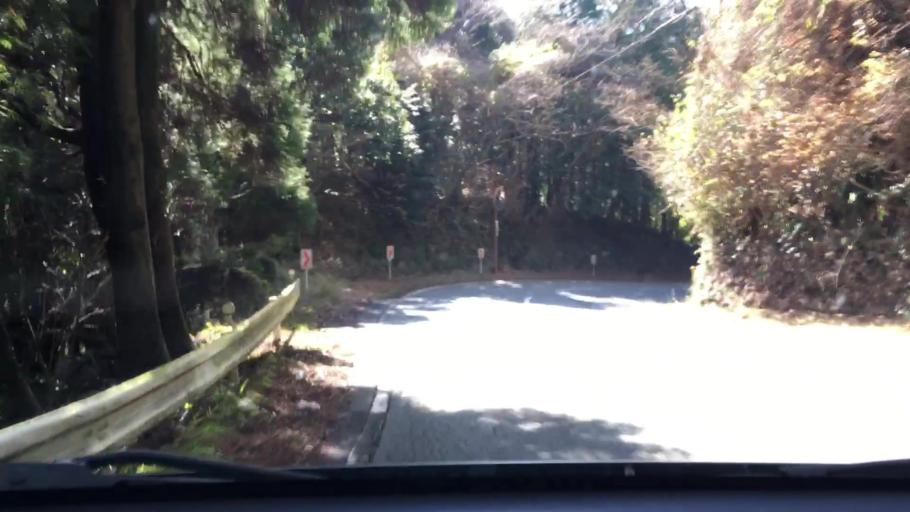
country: JP
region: Kagoshima
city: Ijuin
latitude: 31.7130
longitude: 130.4238
